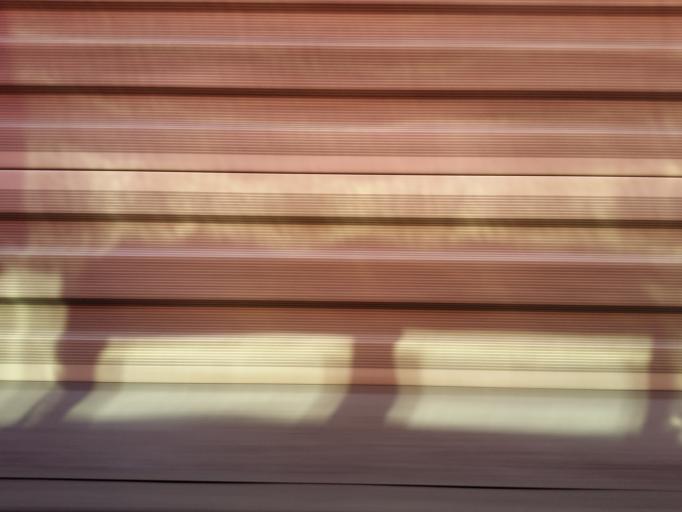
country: NO
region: Oslo
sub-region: Oslo
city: Oslo
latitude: 59.8787
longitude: 10.7754
